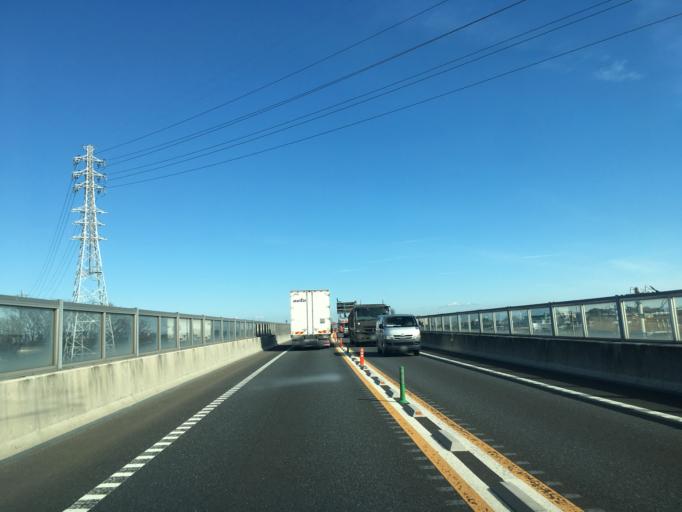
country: JP
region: Saitama
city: Kukichuo
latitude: 36.0521
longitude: 139.6878
